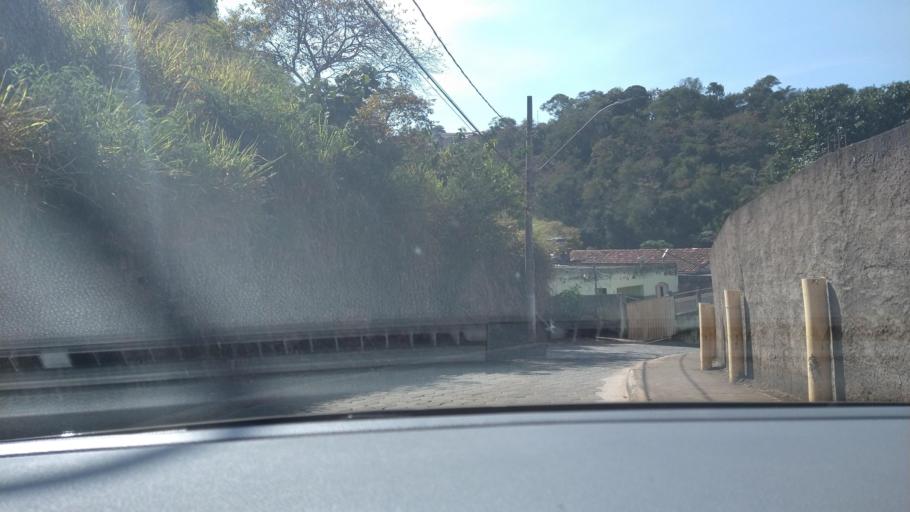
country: BR
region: Minas Gerais
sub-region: Rio Piracicaba
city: Rio Piracicaba
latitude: -19.9290
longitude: -43.1743
